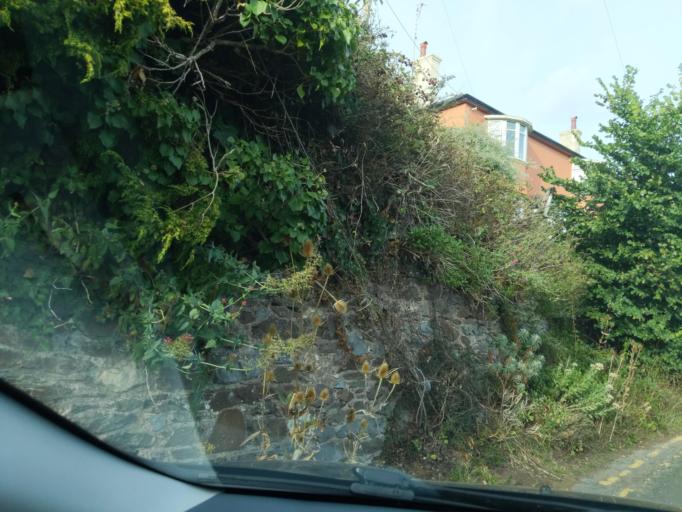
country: GB
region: England
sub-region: Cornwall
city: Millbrook
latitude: 50.3321
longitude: -4.2047
